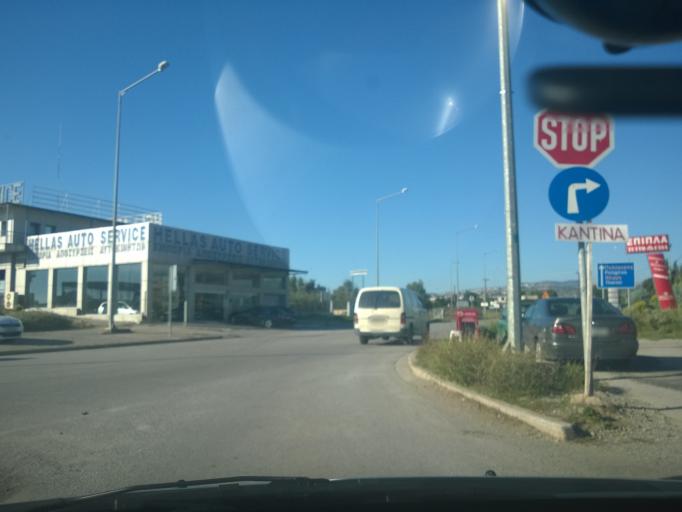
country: GR
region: Central Macedonia
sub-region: Nomos Thessalonikis
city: Thermi
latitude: 40.5317
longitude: 23.0137
